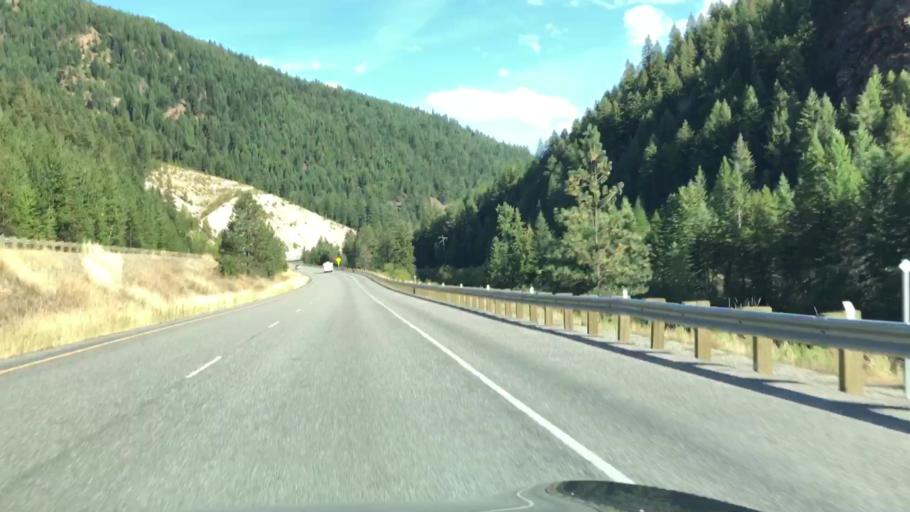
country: US
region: Montana
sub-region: Sanders County
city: Thompson Falls
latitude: 47.3130
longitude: -115.2187
